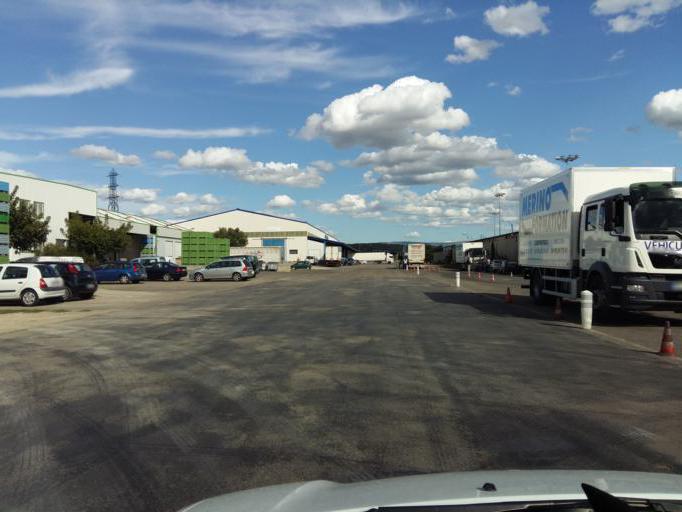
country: FR
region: Provence-Alpes-Cote d'Azur
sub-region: Departement du Vaucluse
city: Carpentras
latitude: 44.0354
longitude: 5.0413
